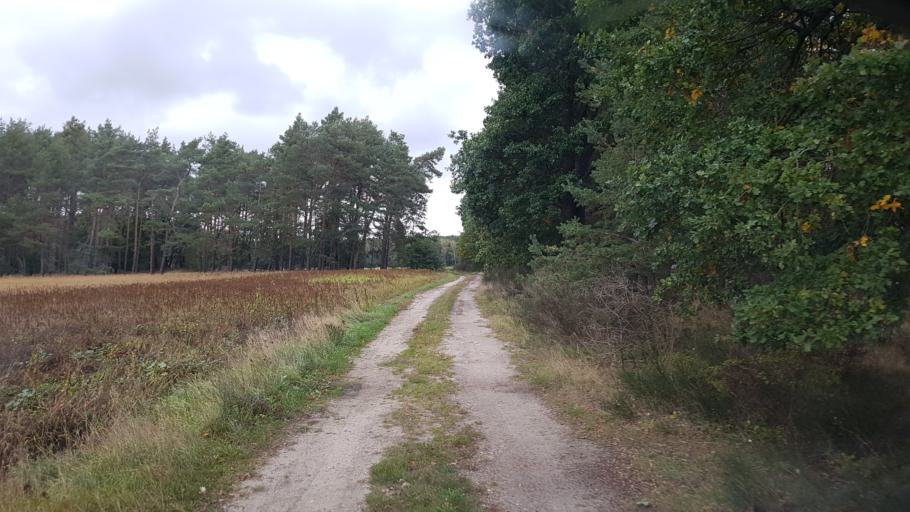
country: DE
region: Brandenburg
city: Finsterwalde
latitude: 51.5763
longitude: 13.6721
